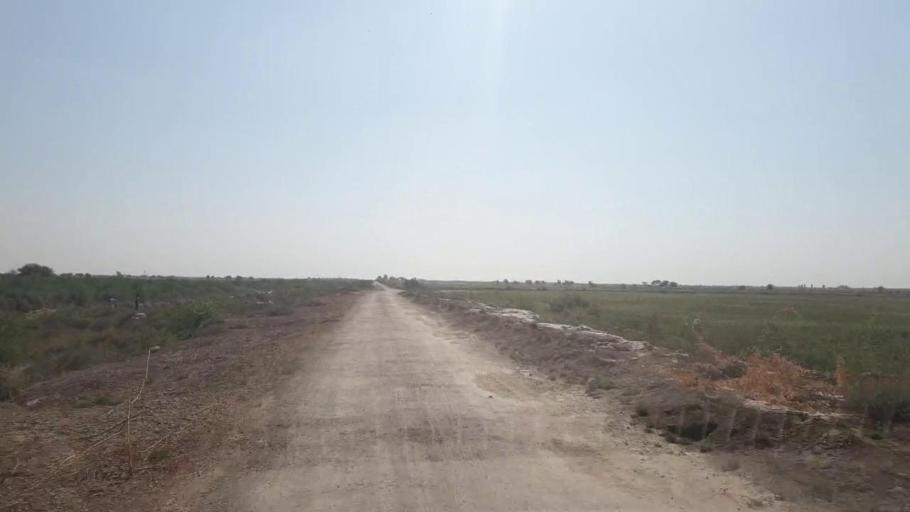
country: PK
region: Sindh
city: Tando Bago
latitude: 24.8623
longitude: 69.1643
